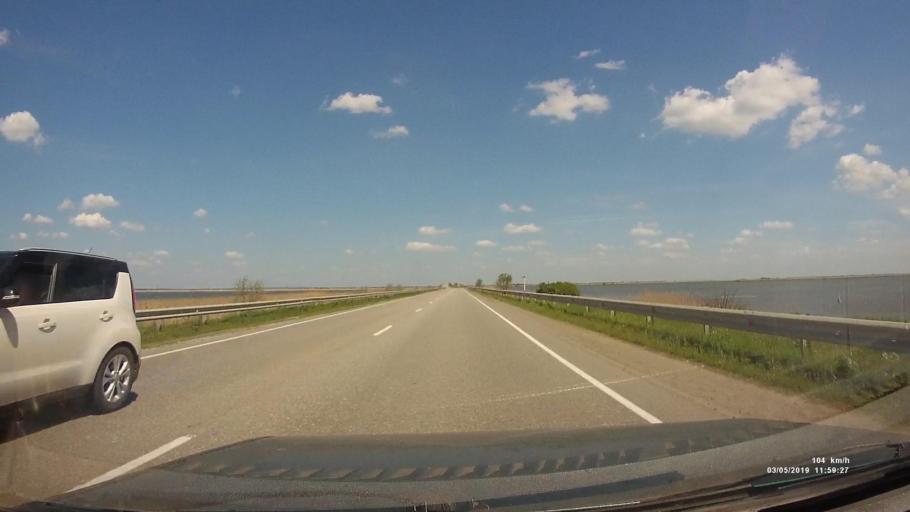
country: RU
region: Rostov
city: Bagayevskaya
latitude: 47.2350
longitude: 40.3305
